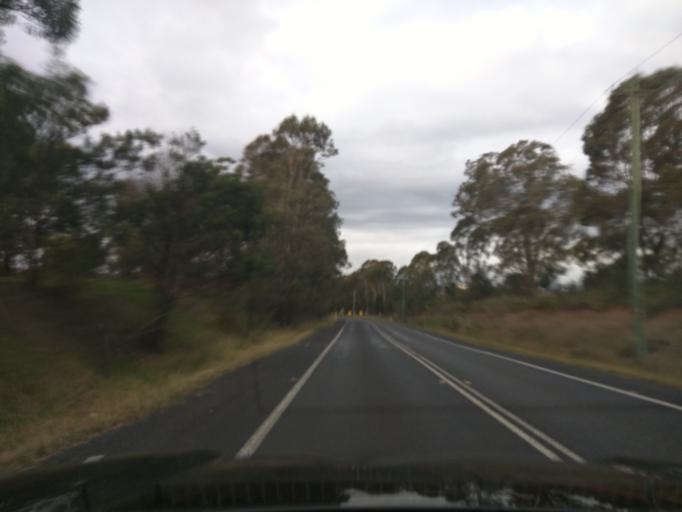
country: AU
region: New South Wales
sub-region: Wollondilly
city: Douglas Park
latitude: -34.2213
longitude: 150.7660
